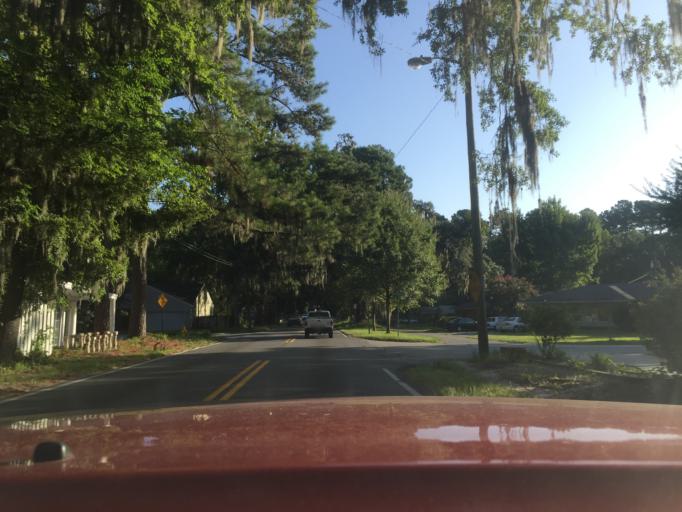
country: US
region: Georgia
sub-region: Chatham County
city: Isle of Hope
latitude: 32.0145
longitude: -81.0983
